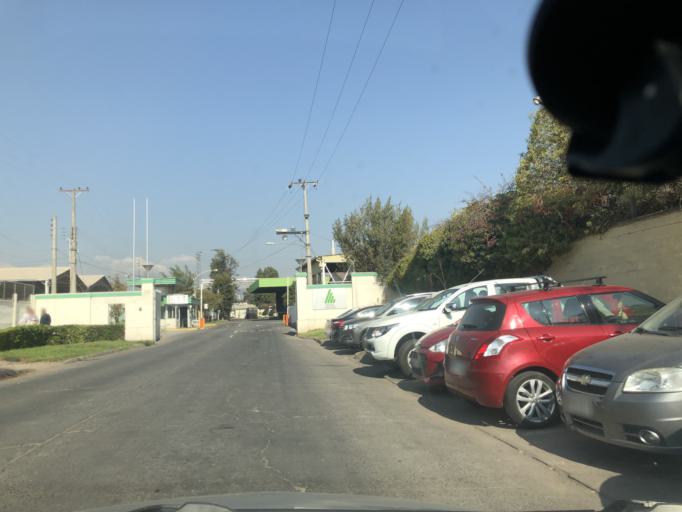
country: CL
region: Santiago Metropolitan
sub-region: Provincia de Cordillera
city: Puente Alto
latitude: -33.6078
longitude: -70.5642
